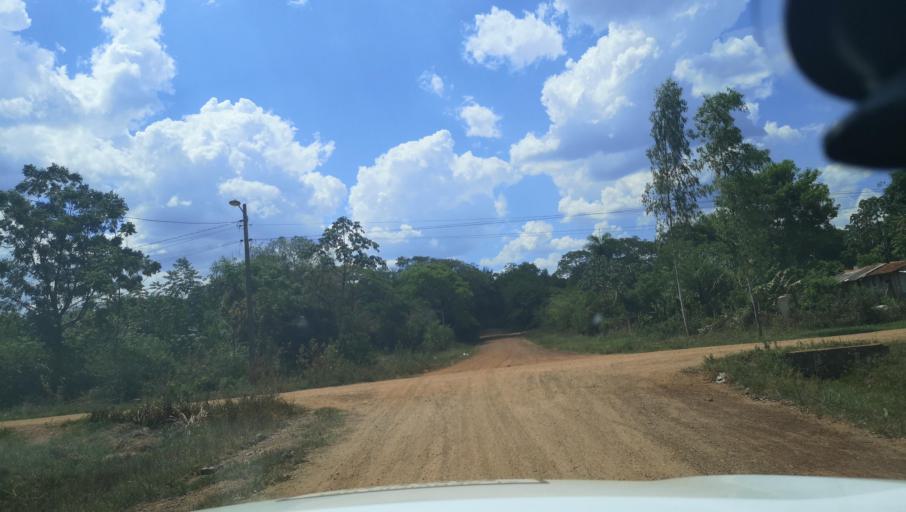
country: PY
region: Itapua
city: Carmen del Parana
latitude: -27.1631
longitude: -56.2469
